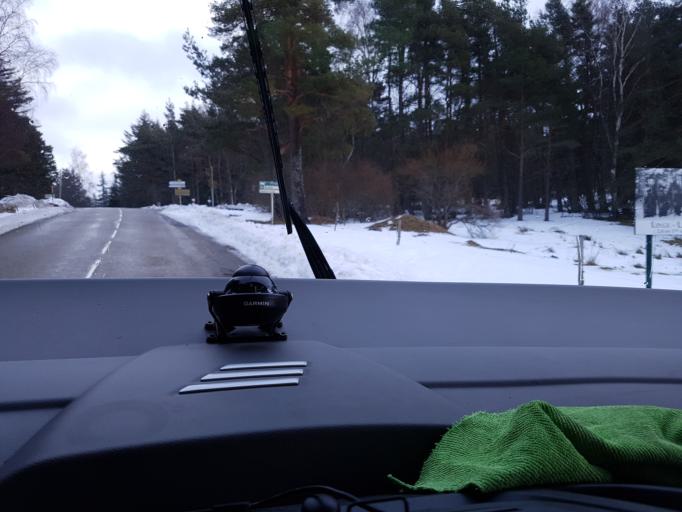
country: FR
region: Alsace
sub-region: Departement du Haut-Rhin
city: Soultzeren
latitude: 48.0878
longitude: 7.1152
